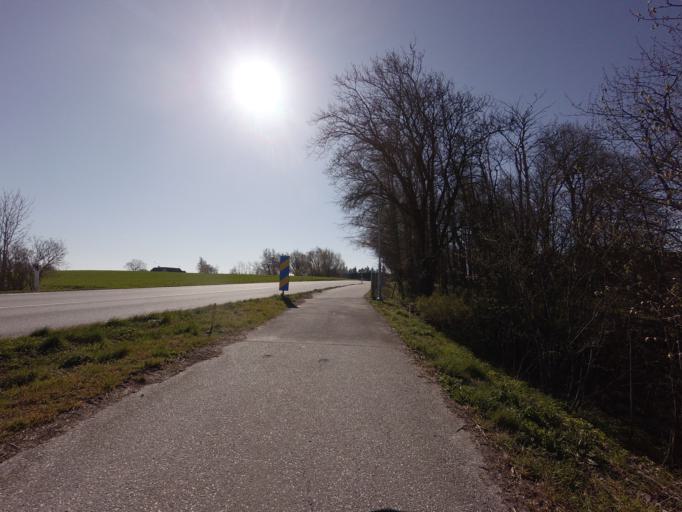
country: SE
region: Skane
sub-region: Malmo
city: Oxie
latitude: 55.4848
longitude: 13.1247
